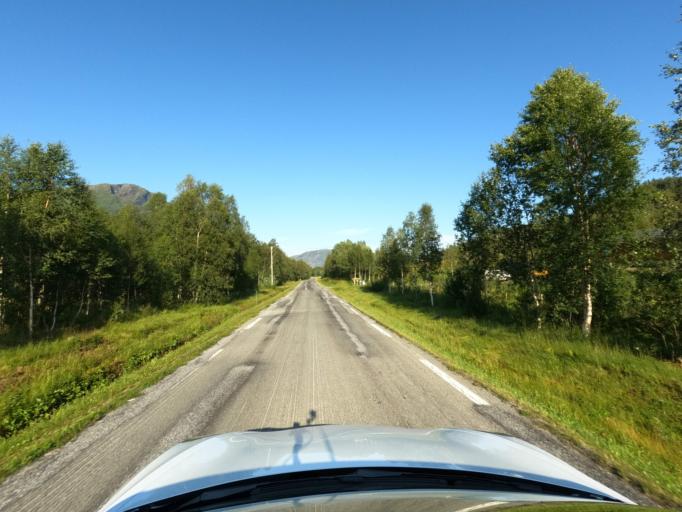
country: NO
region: Nordland
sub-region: Narvik
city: Bjerkvik
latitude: 68.5580
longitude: 17.6358
